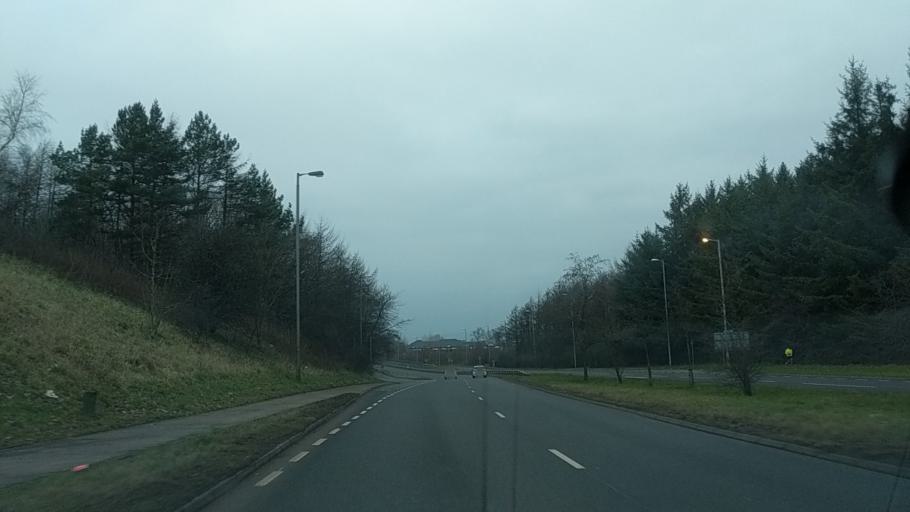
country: GB
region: Scotland
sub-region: Glasgow City
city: Carmunnock
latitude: 55.7684
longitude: -4.2209
